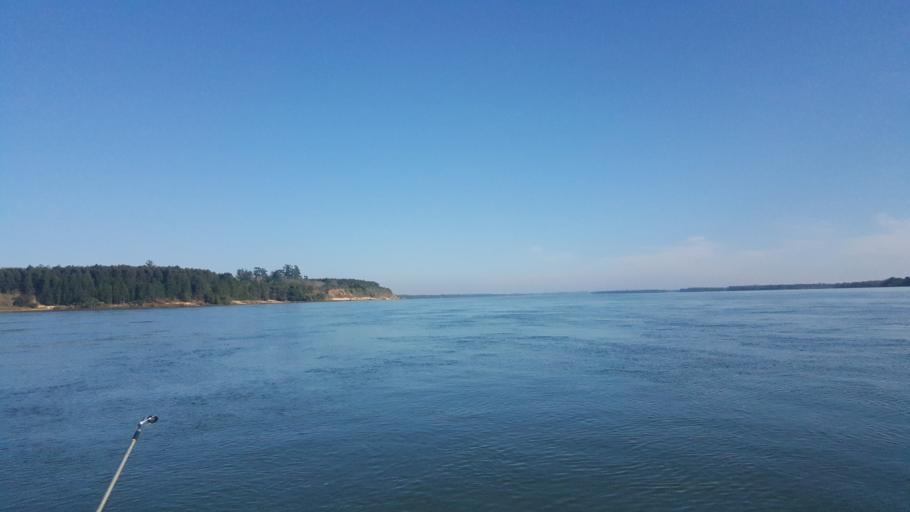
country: AR
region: Corrientes
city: Ituzaingo
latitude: -27.6031
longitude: -56.8562
